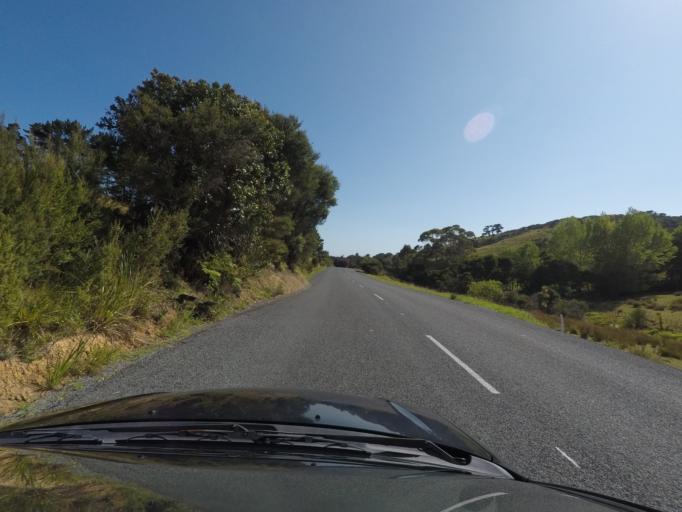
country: NZ
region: Auckland
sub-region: Auckland
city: Warkworth
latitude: -36.2752
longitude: 174.7931
